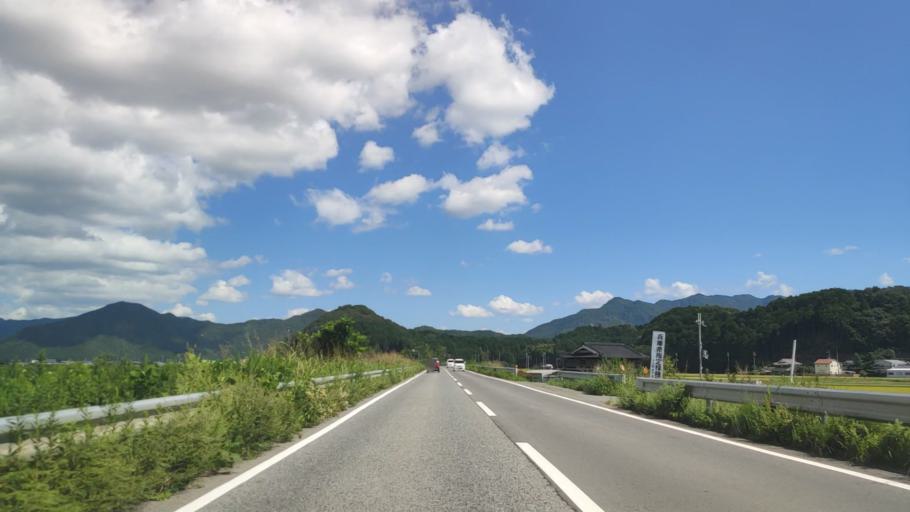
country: JP
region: Hyogo
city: Nishiwaki
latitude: 35.1450
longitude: 135.0326
